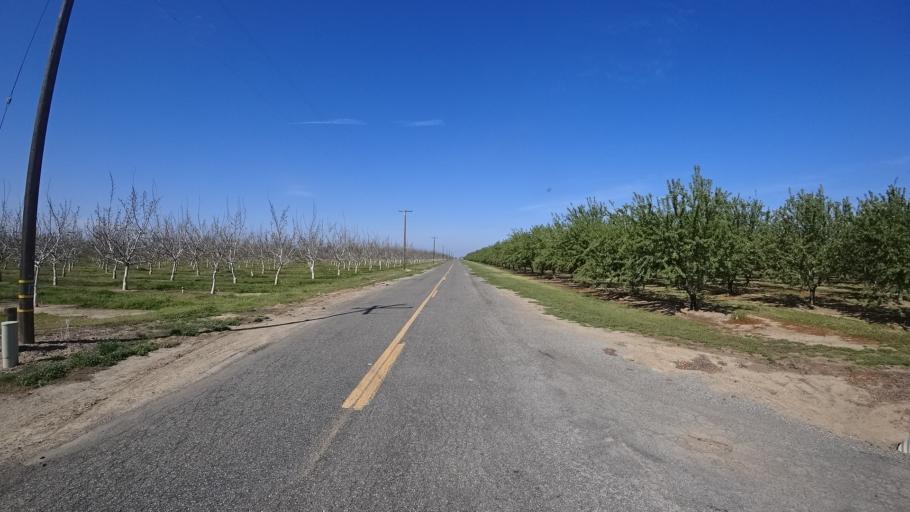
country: US
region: California
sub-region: Glenn County
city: Hamilton City
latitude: 39.6161
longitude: -122.0181
